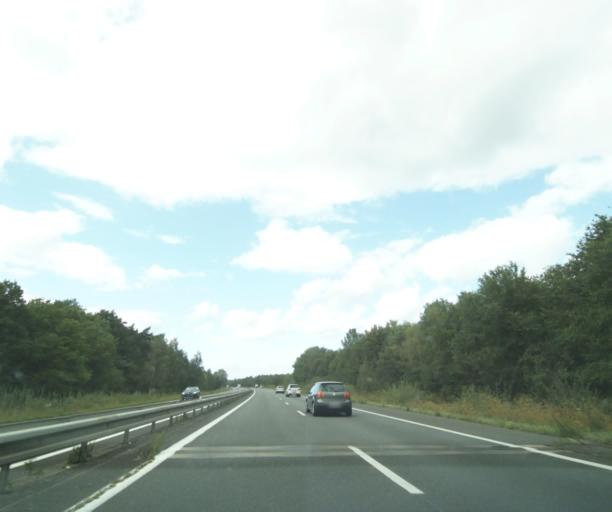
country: FR
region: Centre
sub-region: Departement du Loiret
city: La Ferte-Saint-Aubin
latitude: 47.7127
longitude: 1.8987
